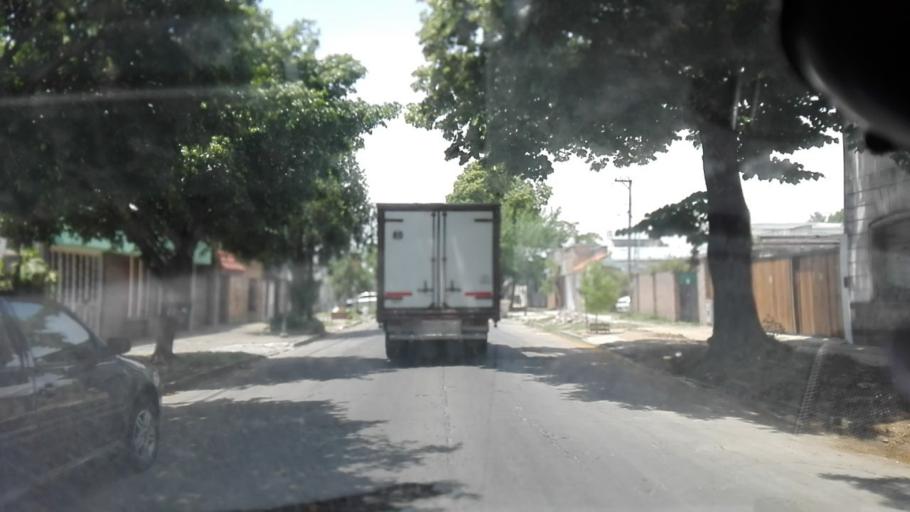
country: AR
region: Buenos Aires
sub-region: Partido de La Plata
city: La Plata
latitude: -34.9206
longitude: -57.9718
